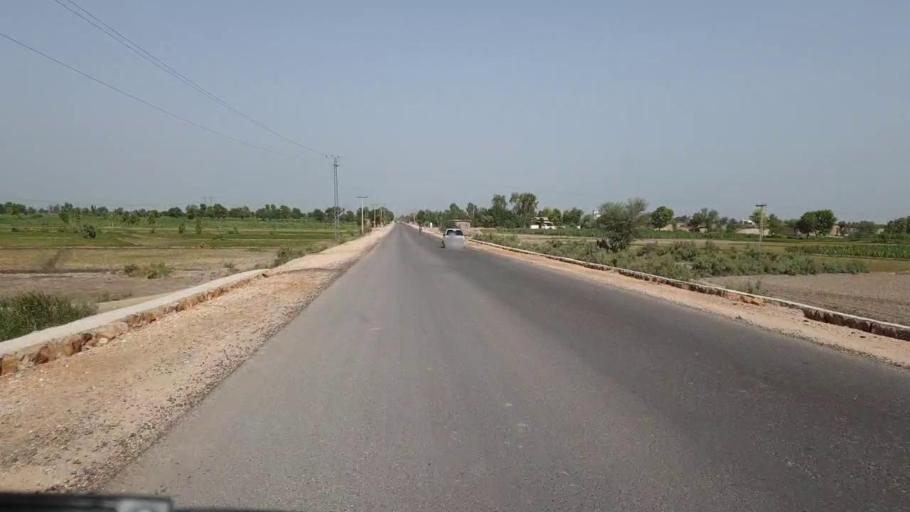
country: PK
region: Sindh
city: Sakrand
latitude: 26.2595
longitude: 68.1876
